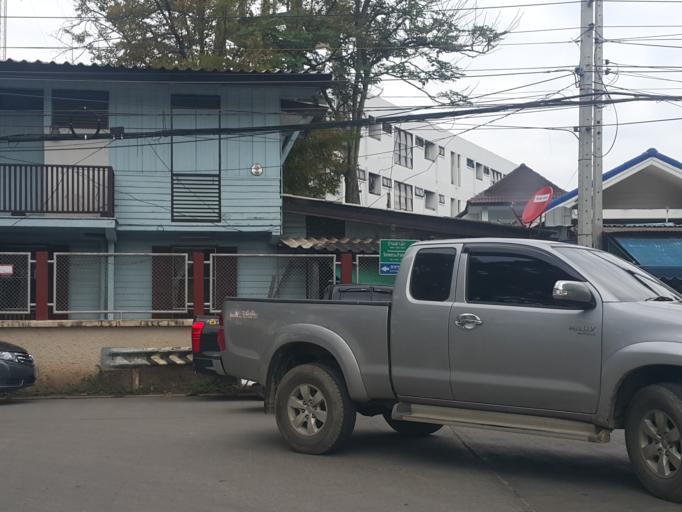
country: TH
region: Lampang
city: Lampang
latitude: 18.2943
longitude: 99.5030
